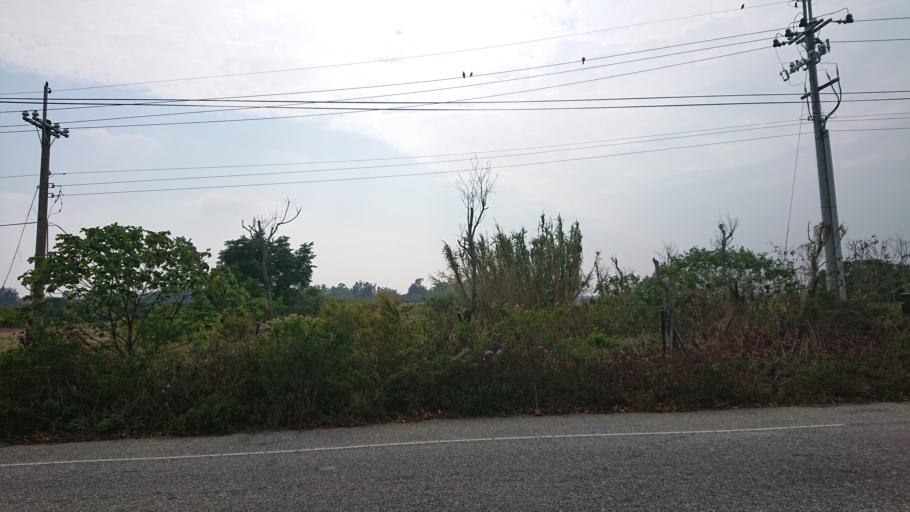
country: TW
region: Fukien
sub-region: Kinmen
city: Jincheng
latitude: 24.4518
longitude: 118.3812
